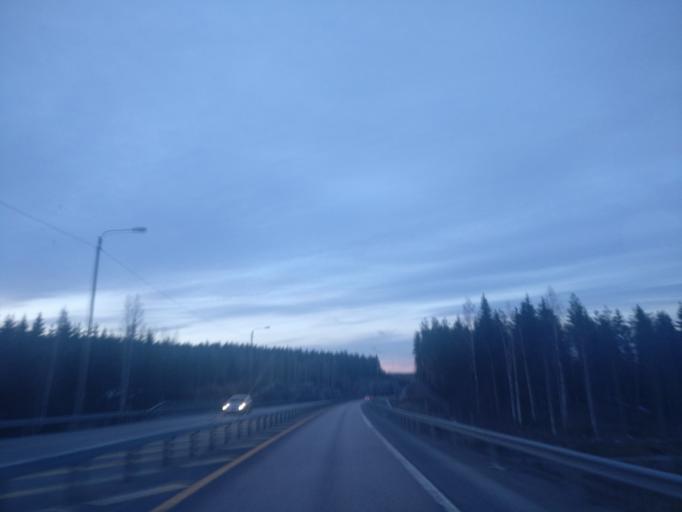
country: FI
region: Central Finland
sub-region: Jyvaeskylae
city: Saeynaetsalo
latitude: 62.2113
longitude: 25.8897
